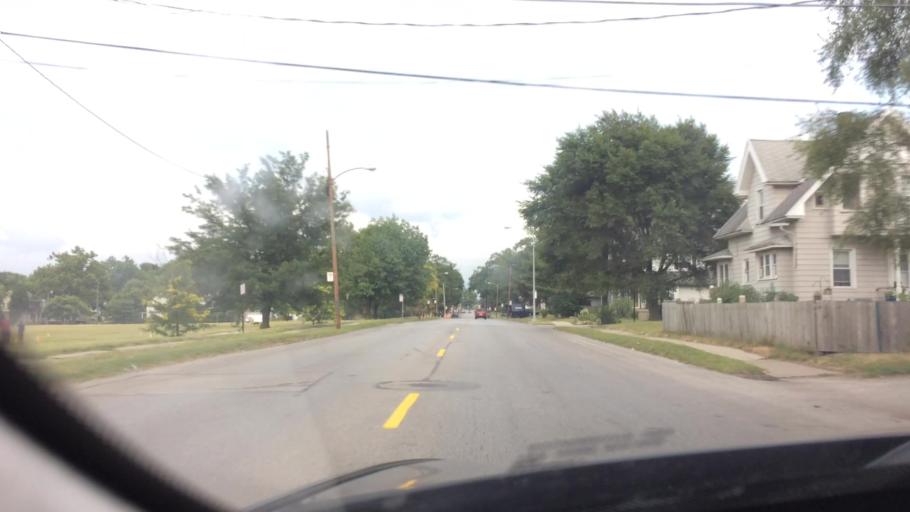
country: US
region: Ohio
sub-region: Wood County
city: Rossford
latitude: 41.6307
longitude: -83.5845
